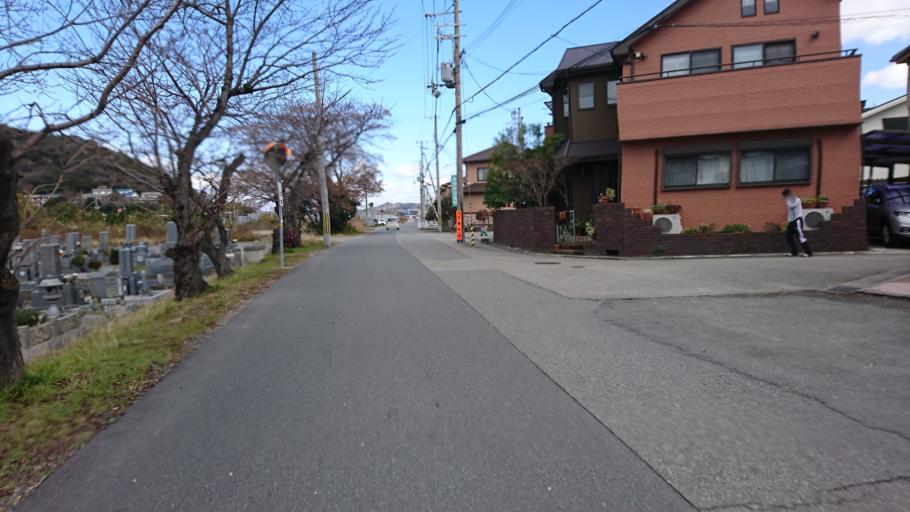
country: JP
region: Hyogo
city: Kakogawacho-honmachi
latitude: 34.7715
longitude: 134.7953
